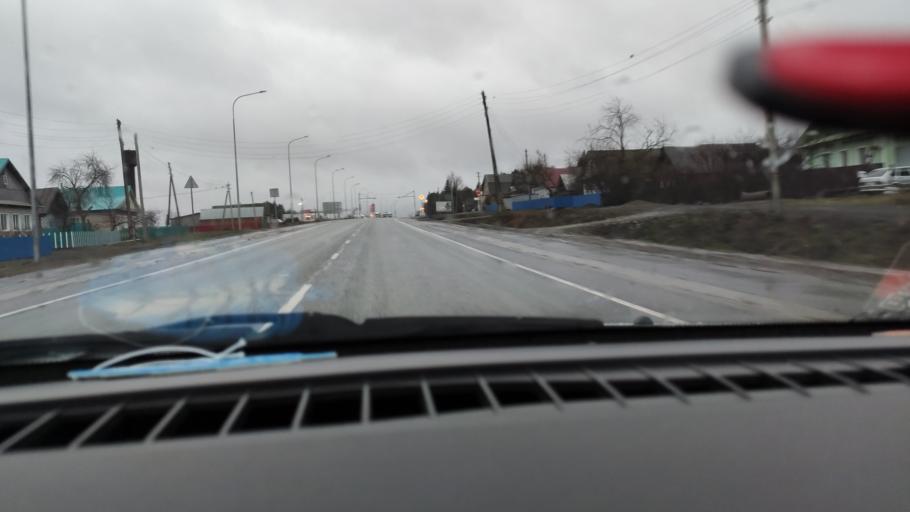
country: RU
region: Tatarstan
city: Mendeleyevsk
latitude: 56.0278
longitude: 52.3708
